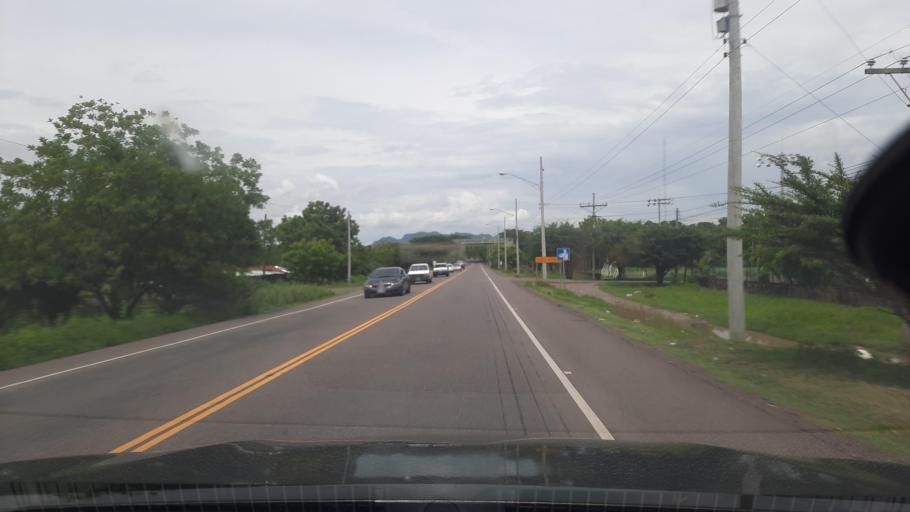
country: HN
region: Valle
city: Nacaome
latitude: 13.5387
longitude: -87.4680
